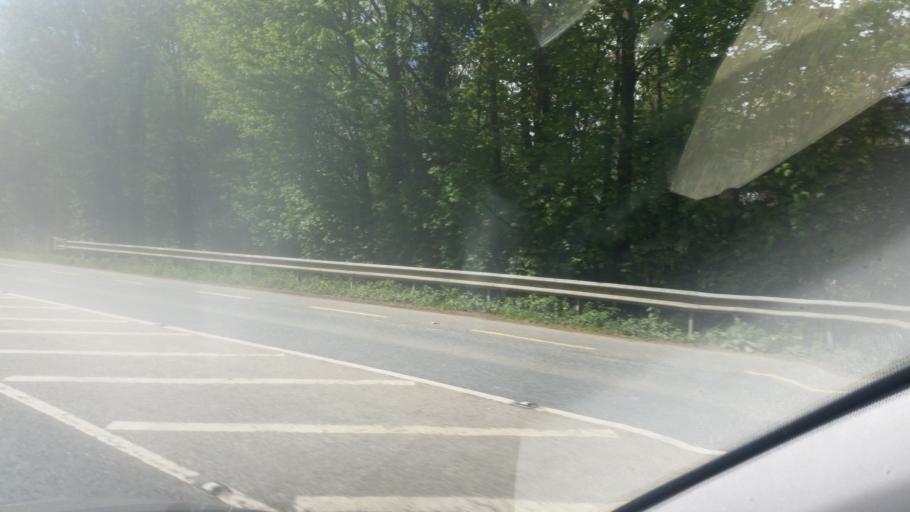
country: IE
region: Leinster
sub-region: Loch Garman
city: Enniscorthy
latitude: 52.4542
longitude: -6.5552
